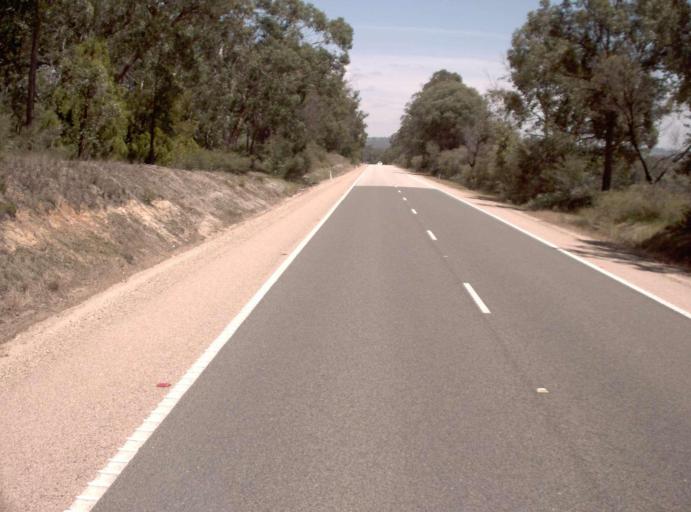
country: AU
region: Victoria
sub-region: East Gippsland
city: Bairnsdale
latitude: -37.7468
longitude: 147.7571
